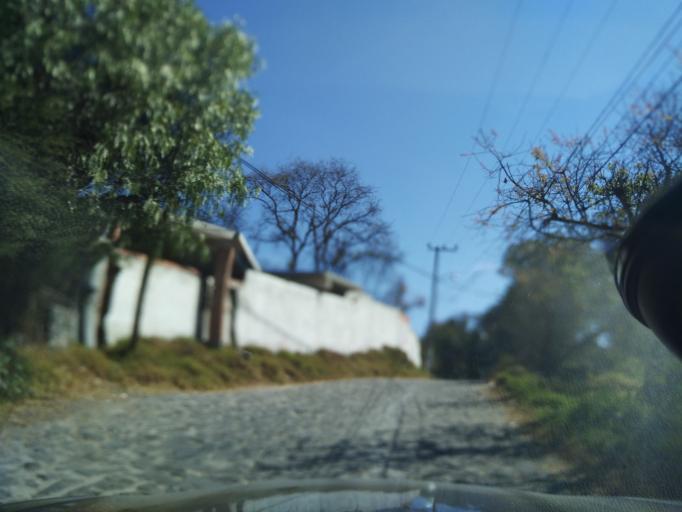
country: MX
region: Mexico
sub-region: Ocoyoacac
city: Colonia el Pirame
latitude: 19.2477
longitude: -99.4735
